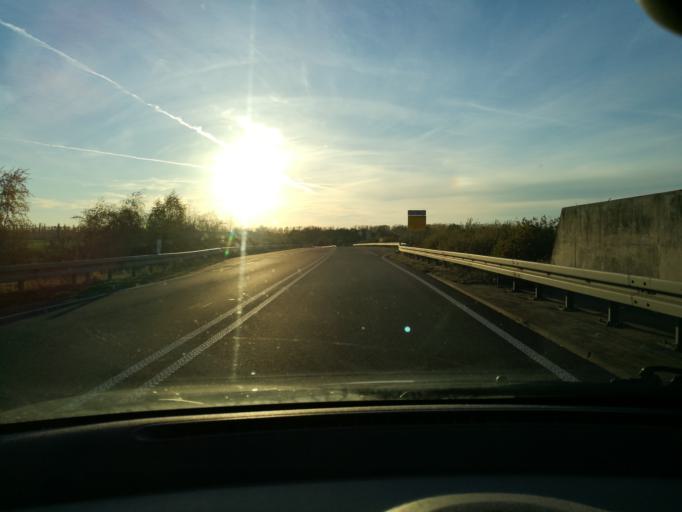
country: DE
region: Brandenburg
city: Perleberg
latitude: 53.0902
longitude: 11.8453
